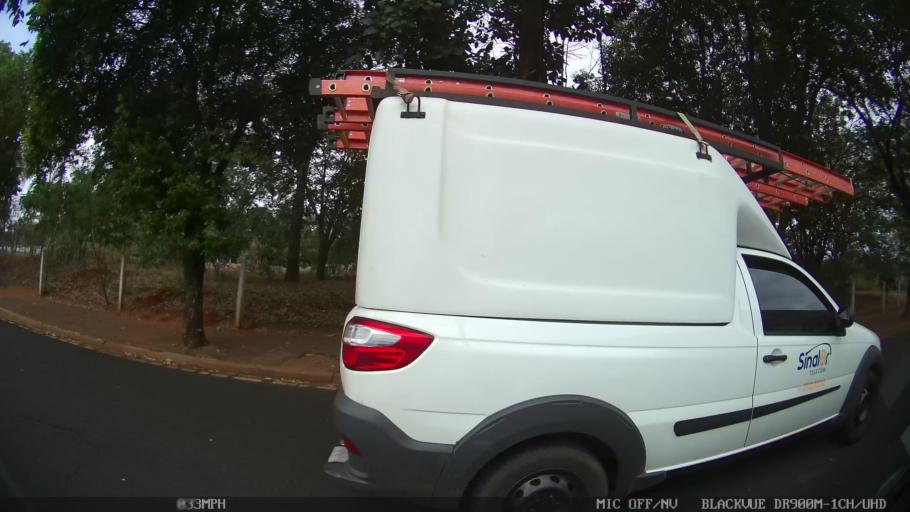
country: BR
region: Sao Paulo
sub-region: Sao Jose Do Rio Preto
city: Sao Jose do Rio Preto
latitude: -20.8233
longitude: -49.3735
